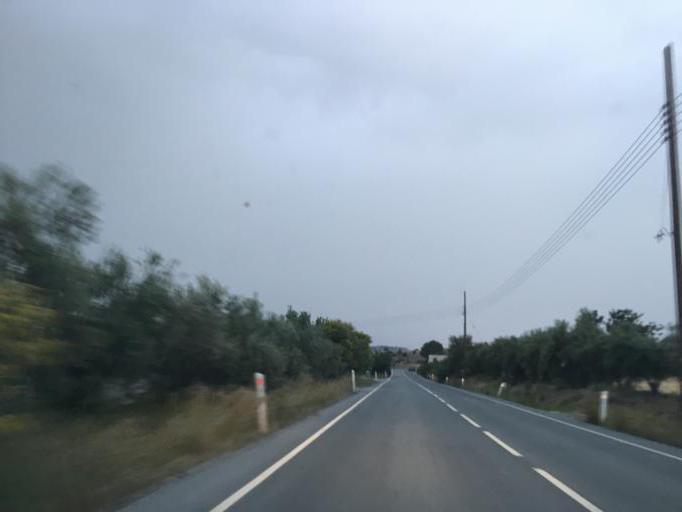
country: CY
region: Limassol
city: Parekklisha
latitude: 34.7691
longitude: 33.1631
